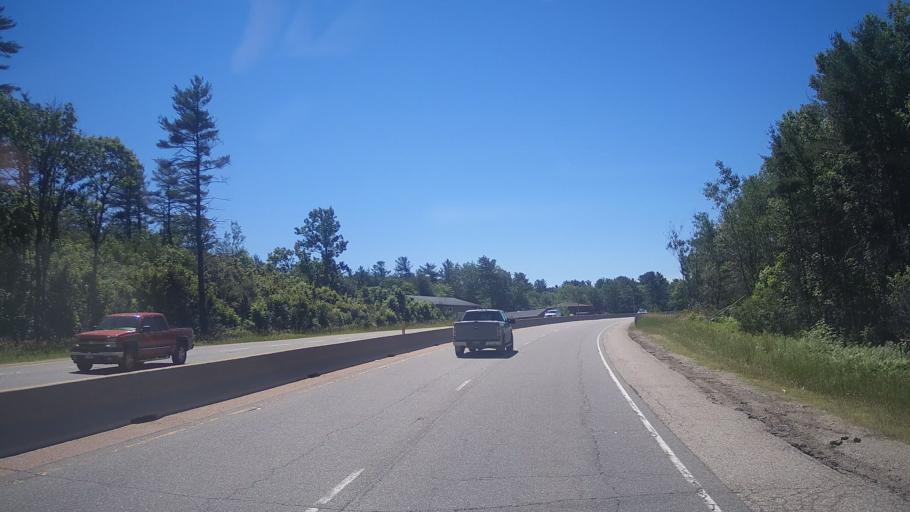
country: CA
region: Ontario
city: Gravenhurst
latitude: 44.8568
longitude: -79.3153
